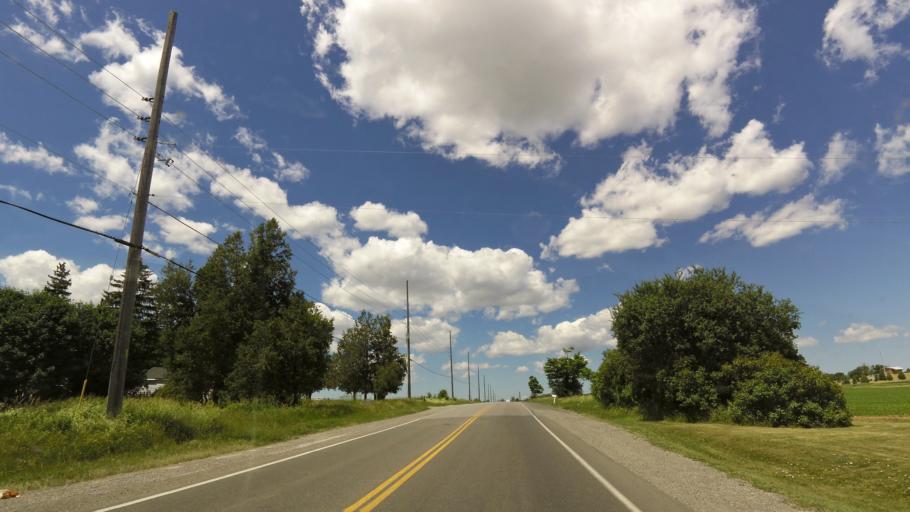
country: CA
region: Ontario
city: Oshawa
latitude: 43.9602
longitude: -78.8586
